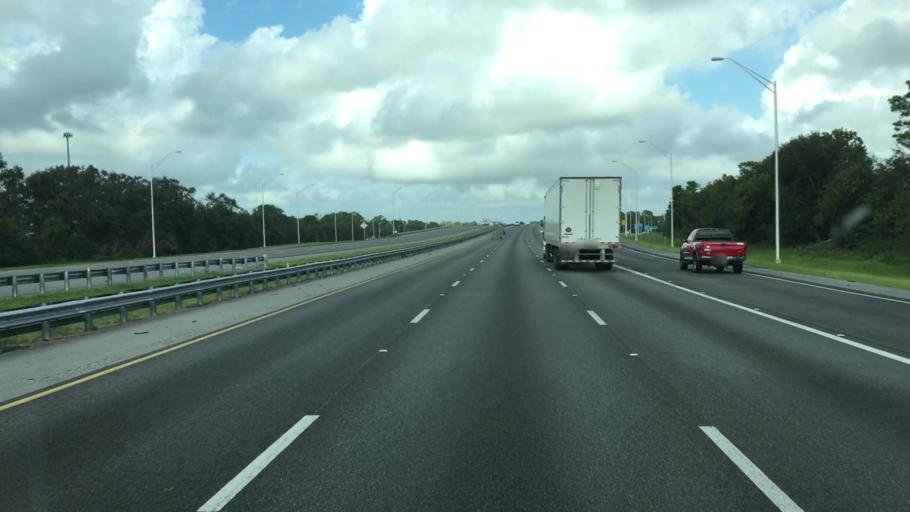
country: US
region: Florida
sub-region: Volusia County
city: Port Orange
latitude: 29.1009
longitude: -81.0260
